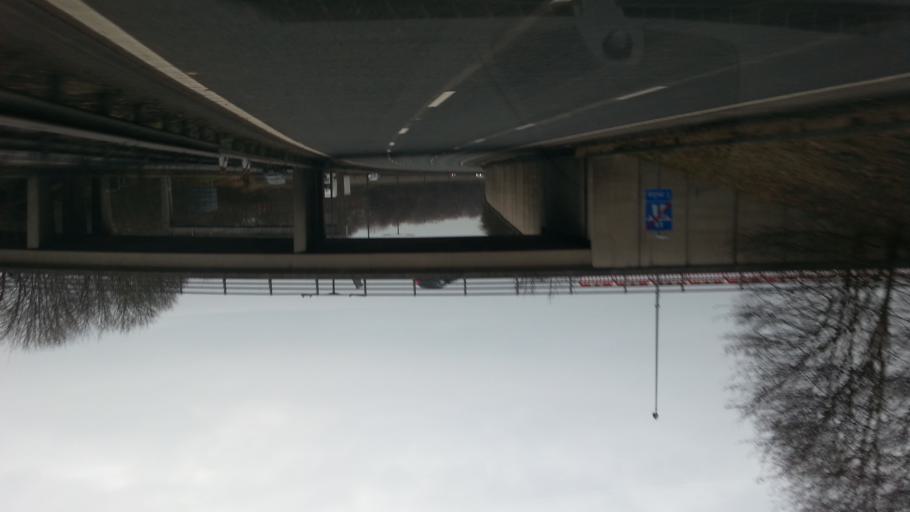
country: GB
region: England
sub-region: Borough of Tameside
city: Denton
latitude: 53.4583
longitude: -2.1081
